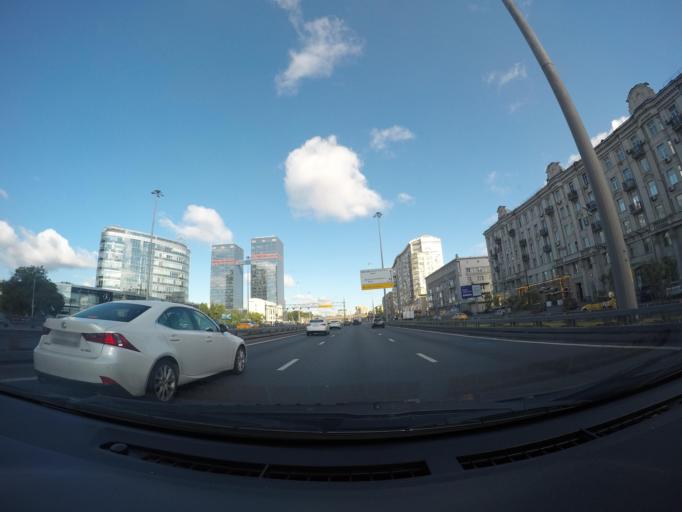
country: RU
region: Moscow
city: Sokol
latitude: 55.7957
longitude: 37.5434
